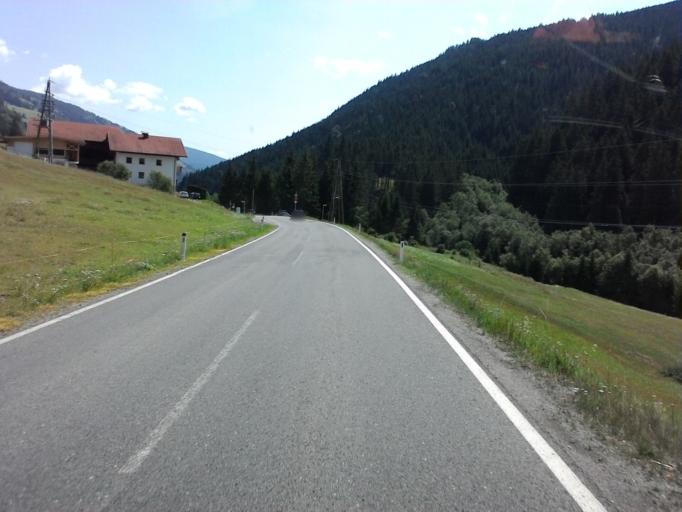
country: AT
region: Tyrol
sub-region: Politischer Bezirk Lienz
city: Untertilliach
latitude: 46.7033
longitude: 12.6870
